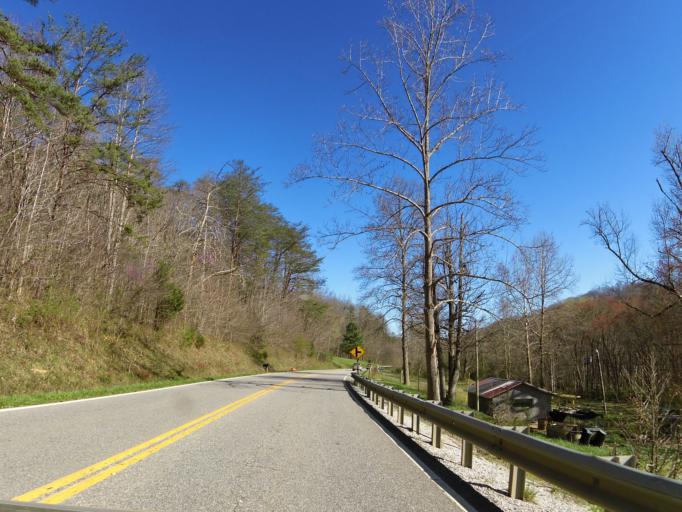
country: US
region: Tennessee
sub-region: Scott County
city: Huntsville
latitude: 36.4472
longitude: -84.4693
